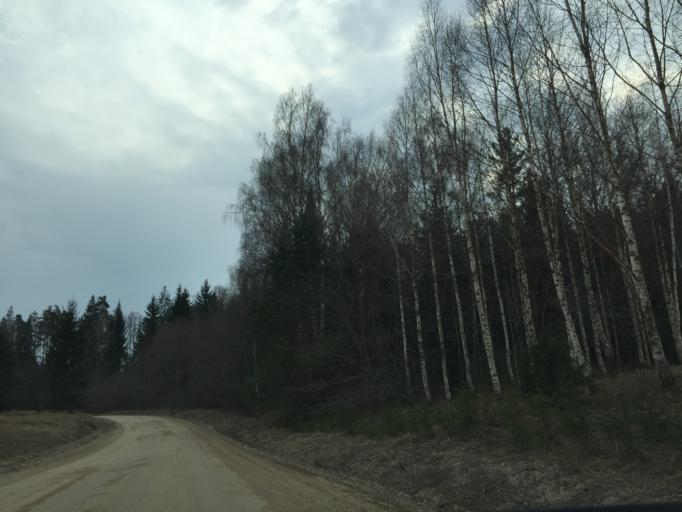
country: LV
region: Amatas Novads
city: Drabesi
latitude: 57.2191
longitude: 25.2295
